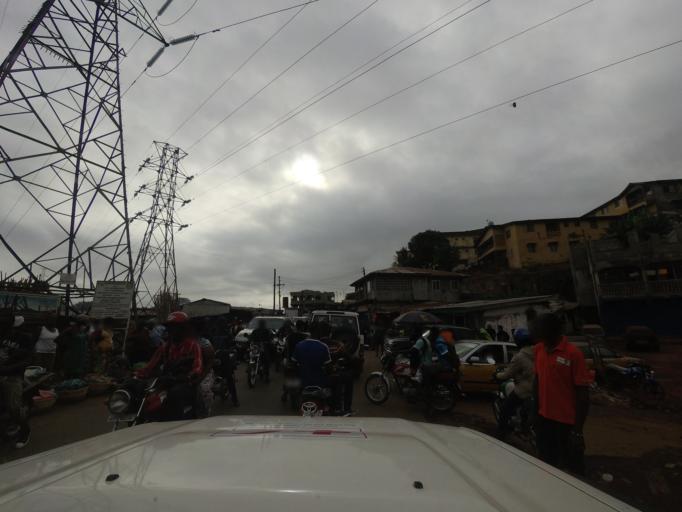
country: SL
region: Western Area
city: Freetown
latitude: 8.4850
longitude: -13.2505
